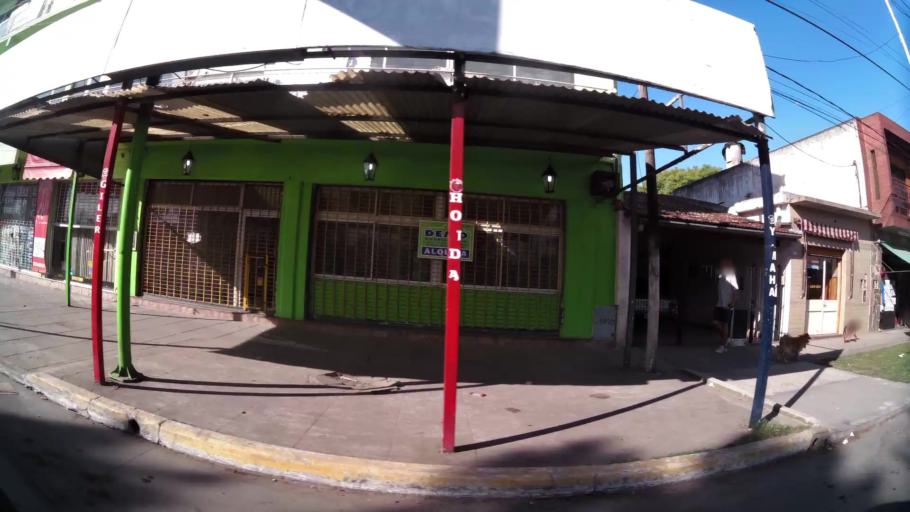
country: AR
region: Buenos Aires
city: Santa Catalina - Dique Lujan
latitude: -34.4860
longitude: -58.7232
